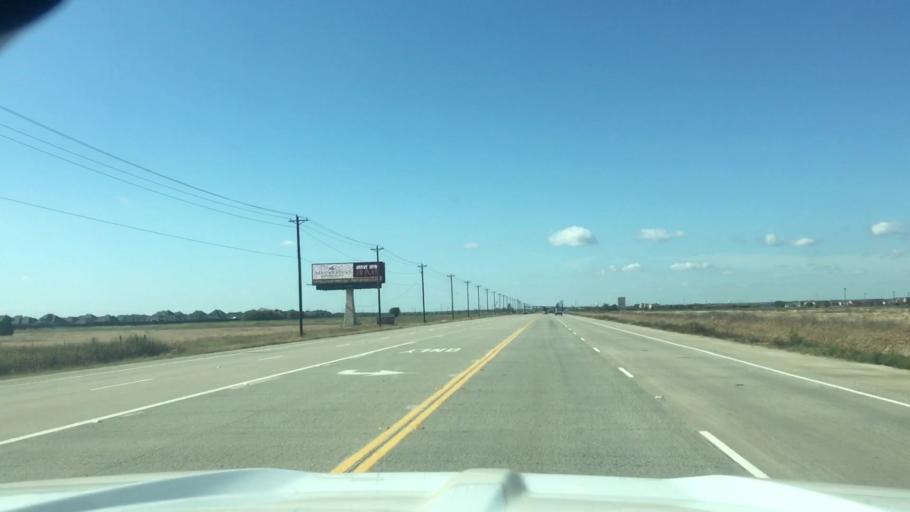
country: US
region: Texas
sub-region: Collin County
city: Prosper
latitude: 33.2192
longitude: -96.8622
